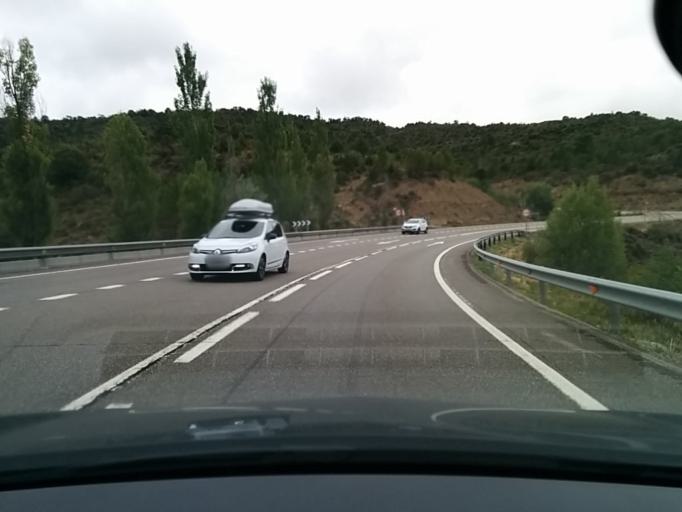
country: ES
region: Aragon
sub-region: Provincia de Huesca
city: Arguis
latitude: 42.3980
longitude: -0.3856
